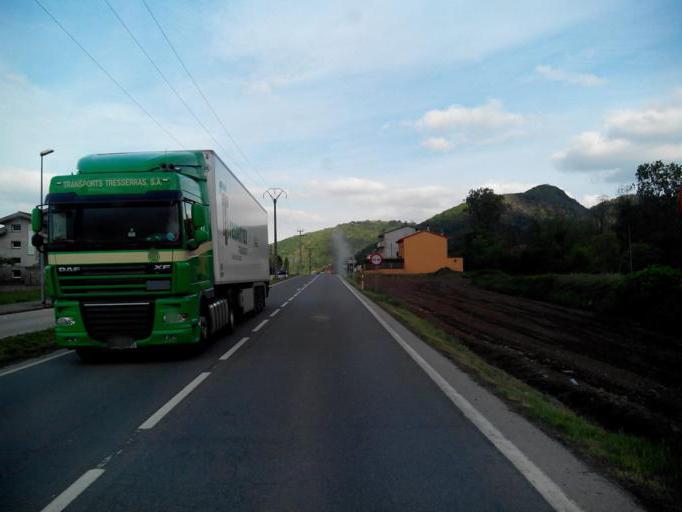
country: ES
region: Catalonia
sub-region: Provincia de Girona
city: MeteOlot
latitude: 42.2085
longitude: 2.4886
